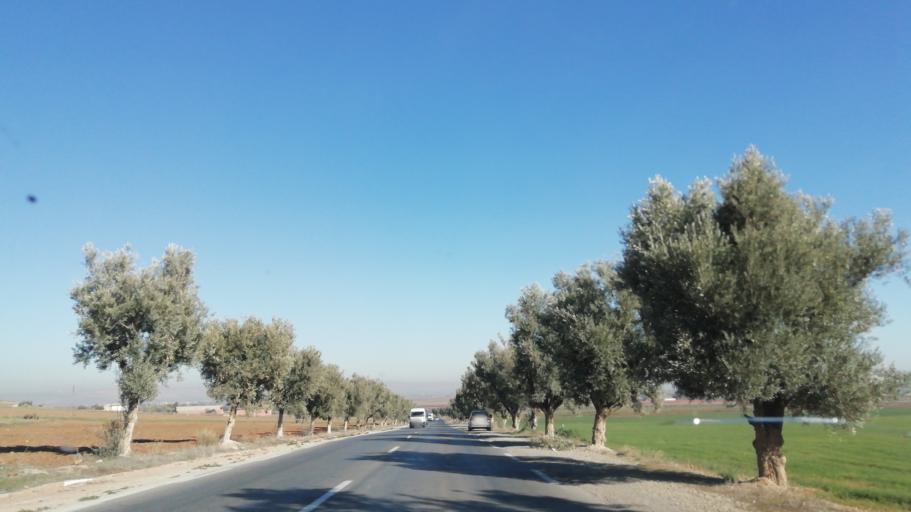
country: DZ
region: Mascara
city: Mascara
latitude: 35.2597
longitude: 0.1274
